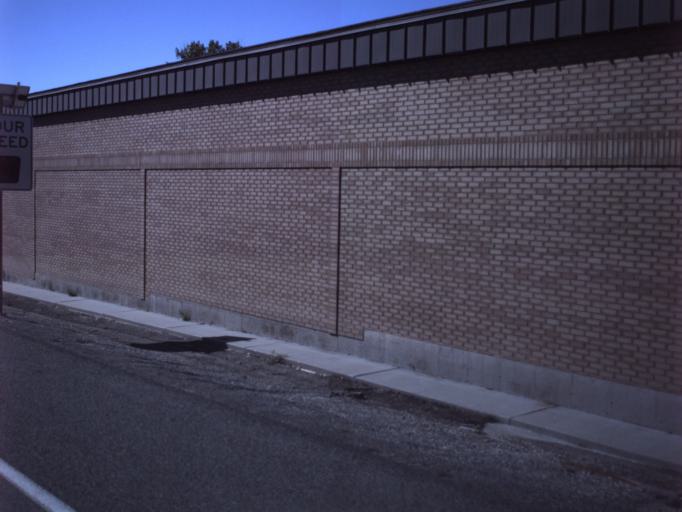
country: US
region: Utah
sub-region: Sanpete County
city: Gunnison
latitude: 39.1605
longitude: -111.8183
